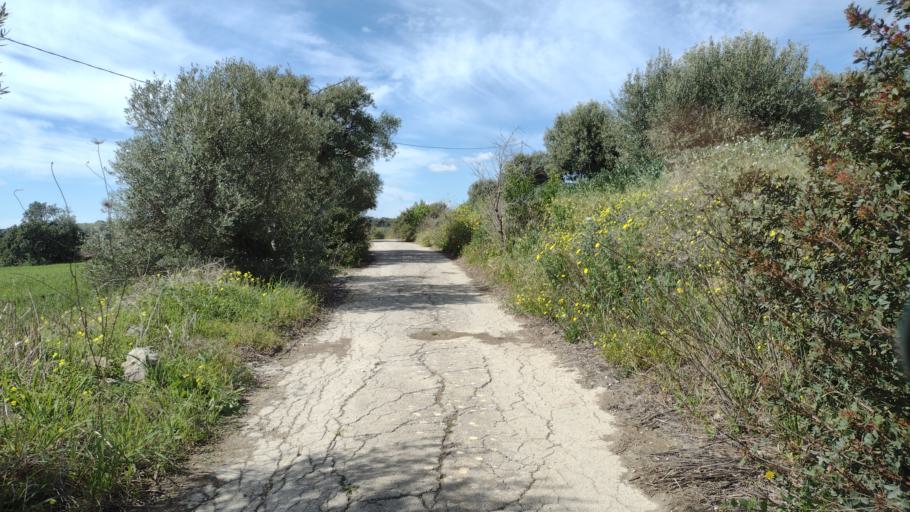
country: IT
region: Sicily
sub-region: Provincia di Siracusa
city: Noto
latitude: 36.9013
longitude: 15.0142
